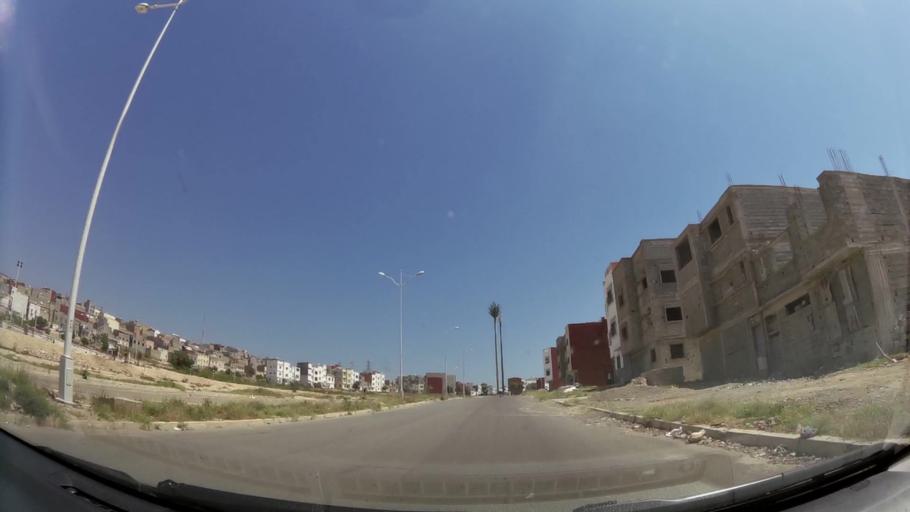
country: MA
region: Oued ed Dahab-Lagouira
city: Dakhla
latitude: 30.4443
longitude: -9.5600
